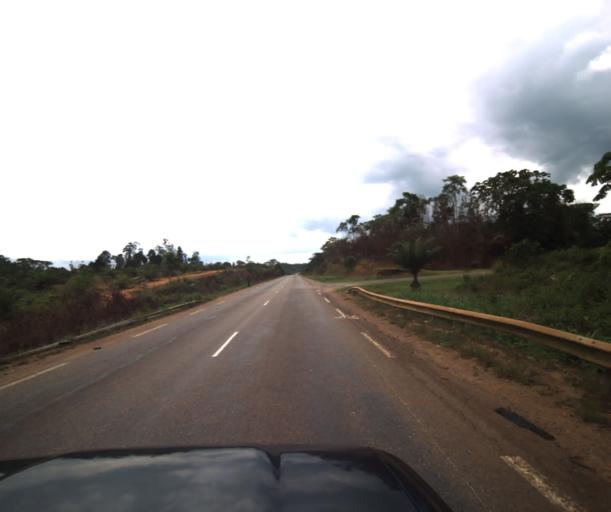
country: CM
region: Littoral
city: Edea
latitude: 3.8670
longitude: 10.0744
